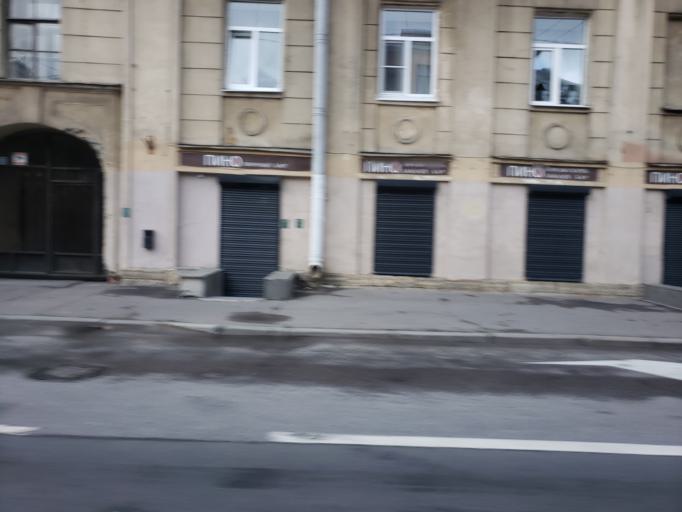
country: RU
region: St.-Petersburg
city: Admiralteisky
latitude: 59.9364
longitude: 30.2828
